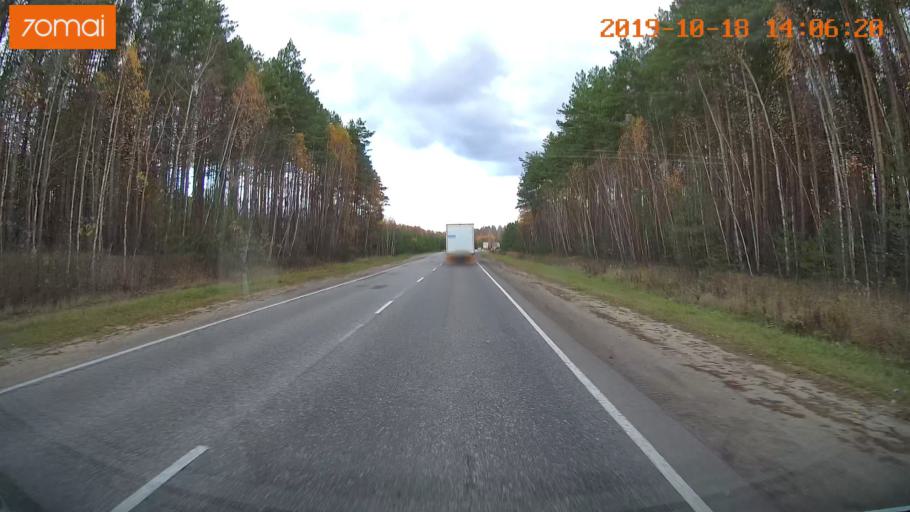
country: RU
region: Rjazan
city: Spas-Klepiki
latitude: 55.1440
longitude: 40.1497
